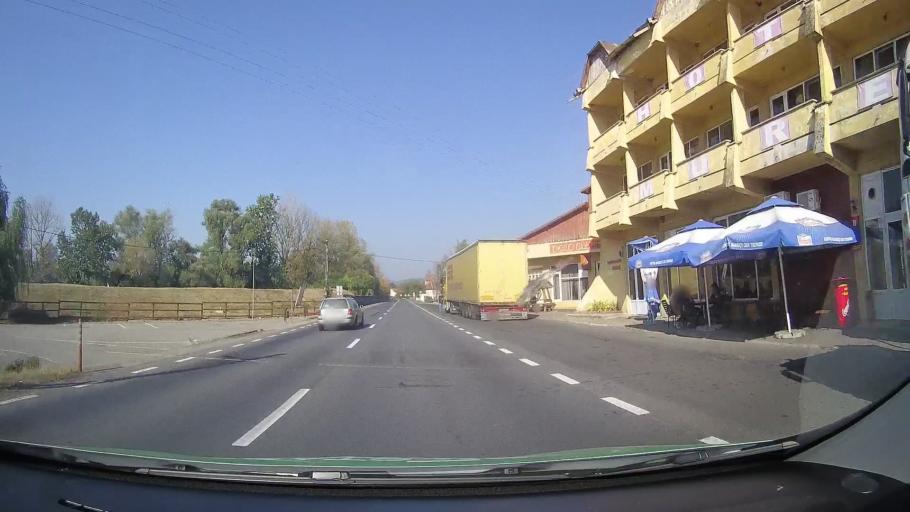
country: RO
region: Hunedoara
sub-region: Comuna Ilia
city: Ilia
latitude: 45.9309
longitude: 22.6570
